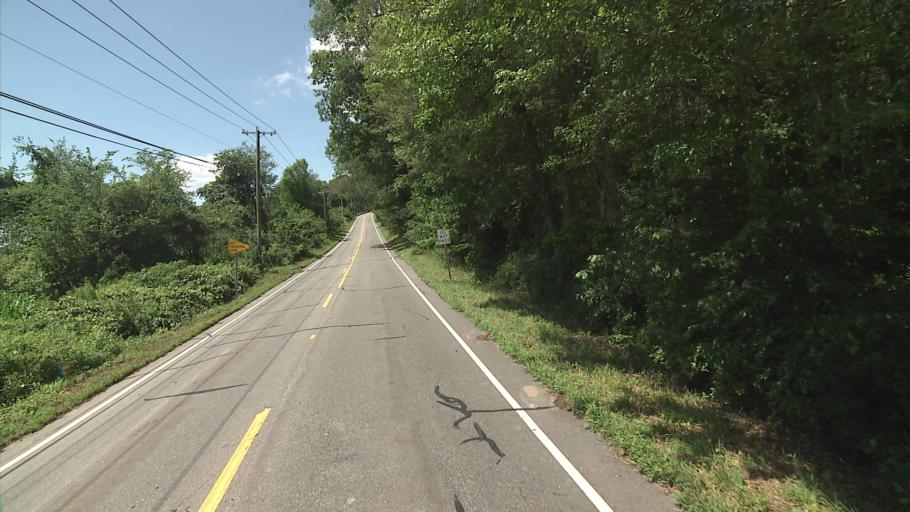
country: US
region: Connecticut
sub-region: New London County
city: Baltic
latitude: 41.6997
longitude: -72.0604
